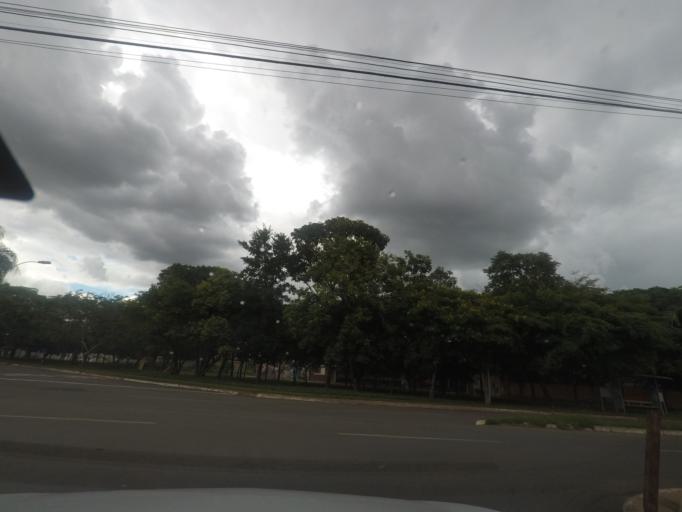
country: BR
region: Goias
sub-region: Goiania
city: Goiania
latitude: -16.6381
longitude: -49.2297
